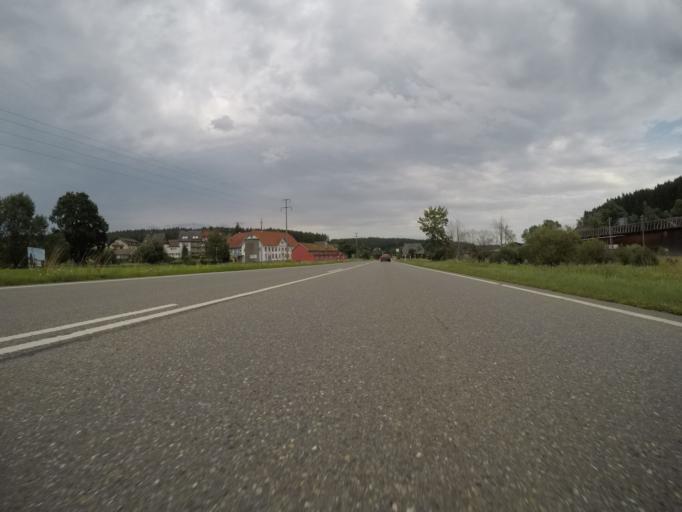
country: DE
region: Baden-Wuerttemberg
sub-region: Freiburg Region
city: Sankt Georgen im Schwarzwald
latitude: 48.1309
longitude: 8.3718
